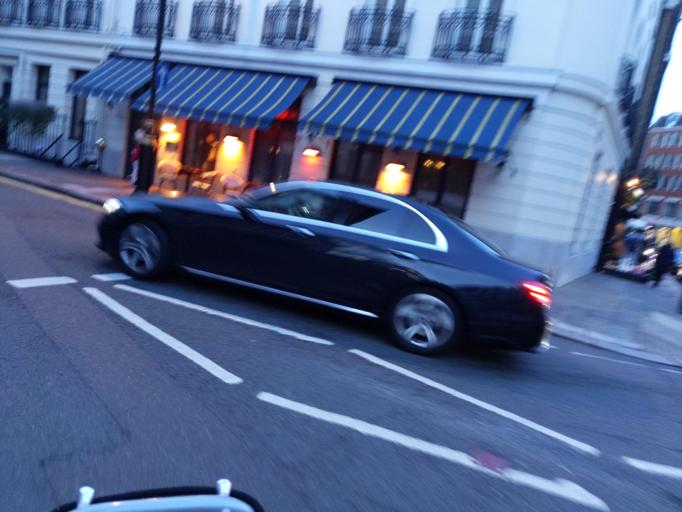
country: GB
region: England
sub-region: Greater London
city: London
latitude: 51.5069
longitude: -0.1470
